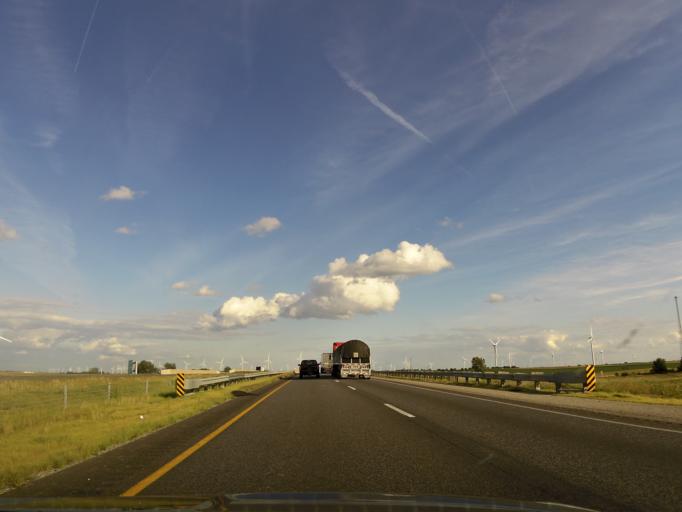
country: US
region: Indiana
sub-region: White County
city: Wolcott
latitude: 40.6683
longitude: -87.0424
